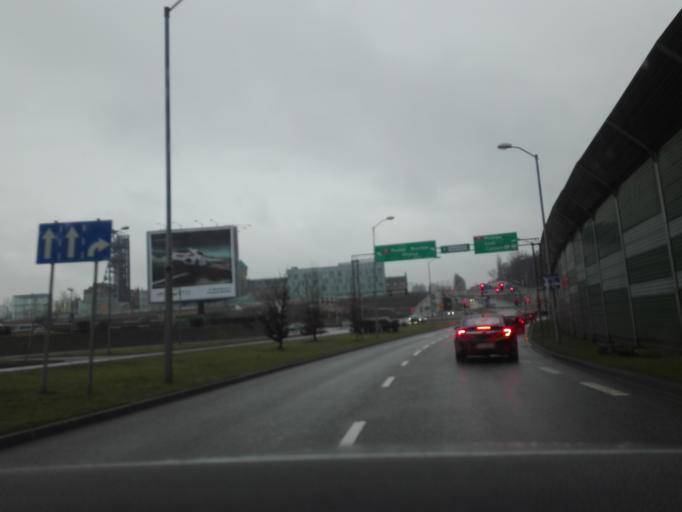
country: PL
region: Silesian Voivodeship
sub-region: Katowice
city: Katowice
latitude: 50.2610
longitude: 19.0352
